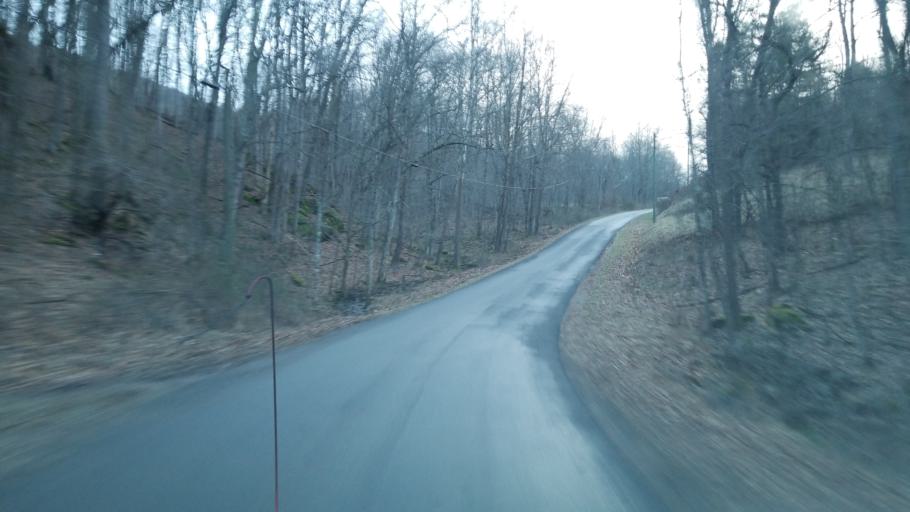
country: US
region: Virginia
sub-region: Pulaski County
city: Pulaski
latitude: 37.1495
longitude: -80.8721
